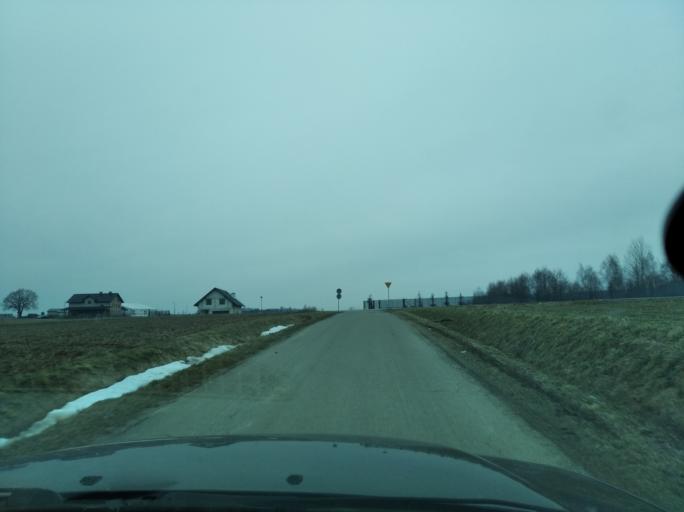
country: PL
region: Subcarpathian Voivodeship
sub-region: Powiat rzeszowski
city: Chmielnik
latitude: 49.9838
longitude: 22.1535
